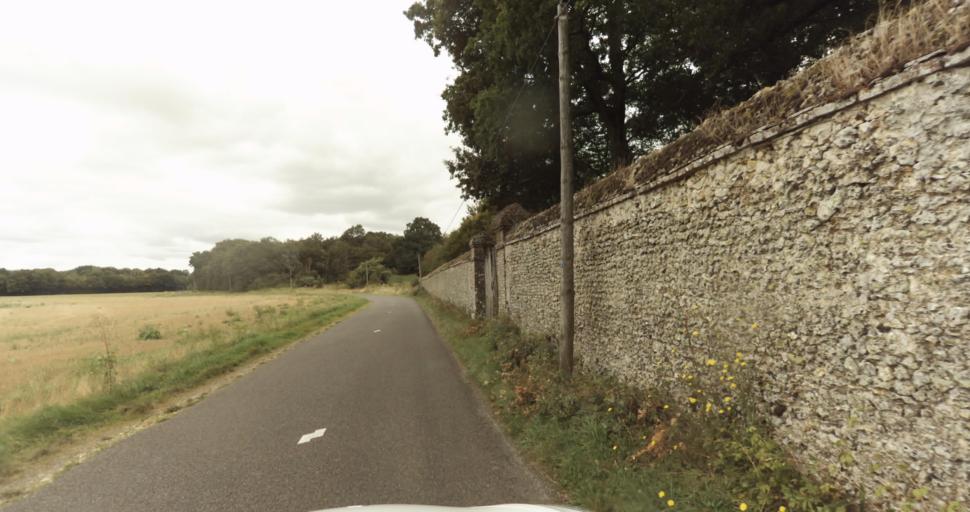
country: FR
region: Centre
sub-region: Departement d'Eure-et-Loir
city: Saint-Lubin-des-Joncherets
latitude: 48.8223
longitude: 1.2341
